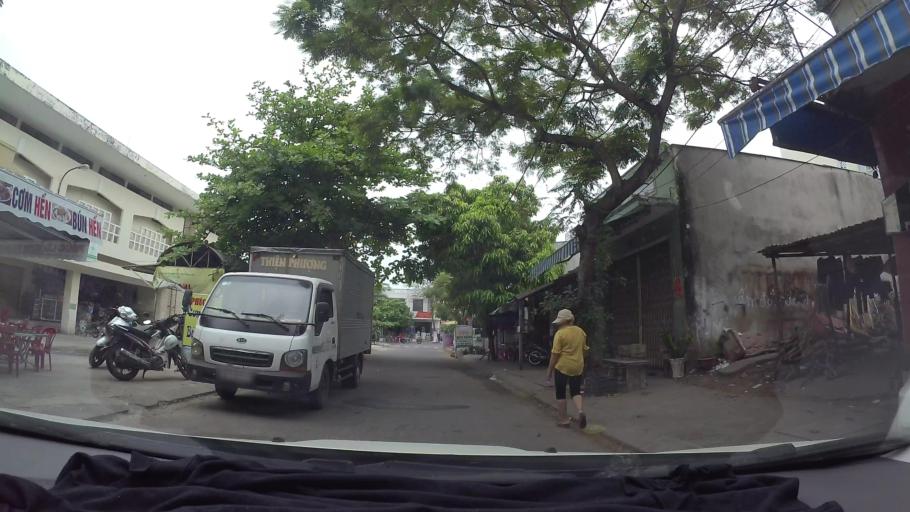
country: VN
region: Da Nang
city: Lien Chieu
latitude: 16.0753
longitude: 108.1724
